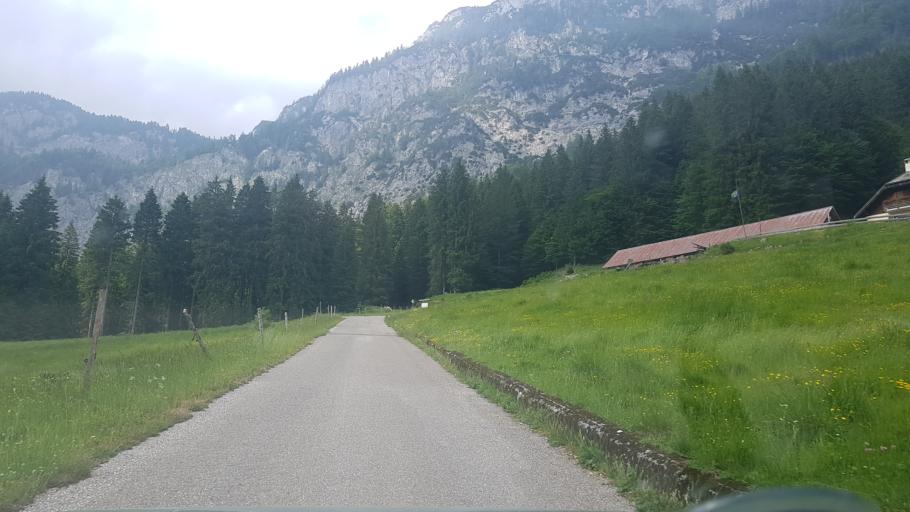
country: IT
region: Friuli Venezia Giulia
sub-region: Provincia di Udine
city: Paularo
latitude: 46.5438
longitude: 13.2043
